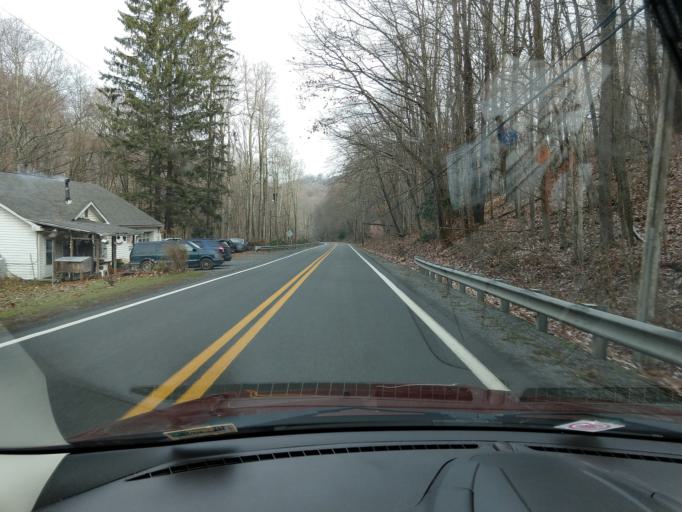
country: US
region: West Virginia
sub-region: Greenbrier County
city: Rainelle
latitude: 38.0684
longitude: -80.7077
